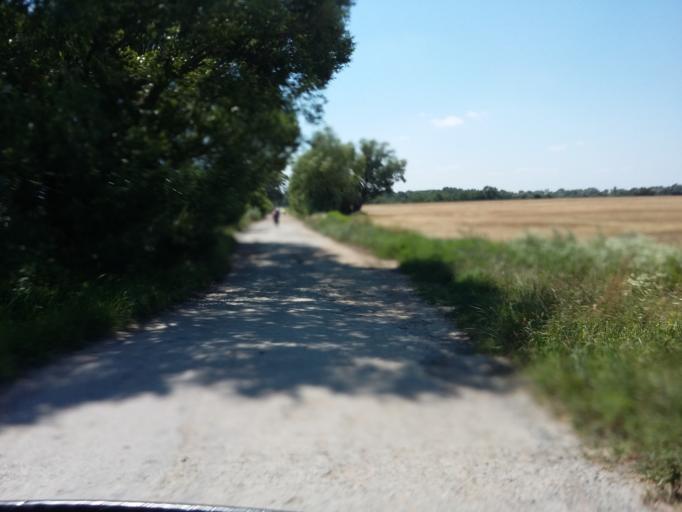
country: AT
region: Lower Austria
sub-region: Politischer Bezirk Ganserndorf
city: Marchegg
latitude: 48.2852
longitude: 16.9678
